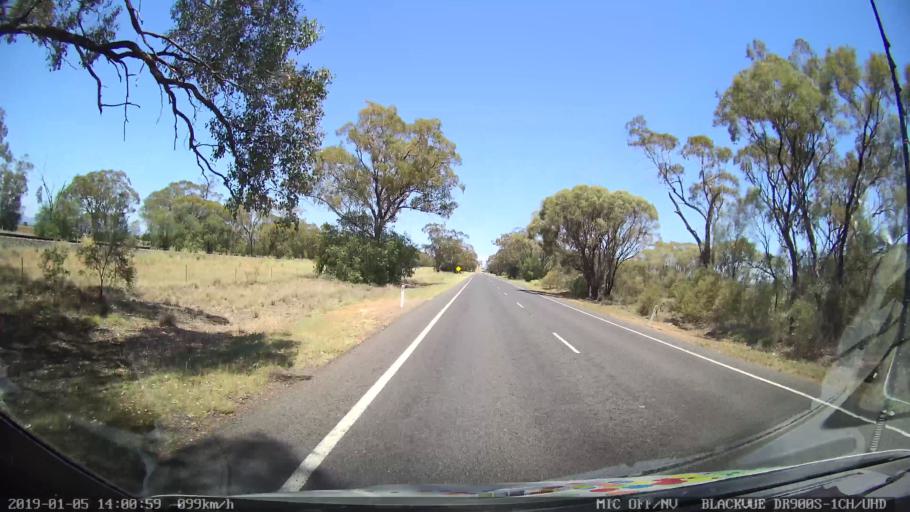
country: AU
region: New South Wales
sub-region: Gunnedah
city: Gunnedah
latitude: -31.1651
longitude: 150.3192
